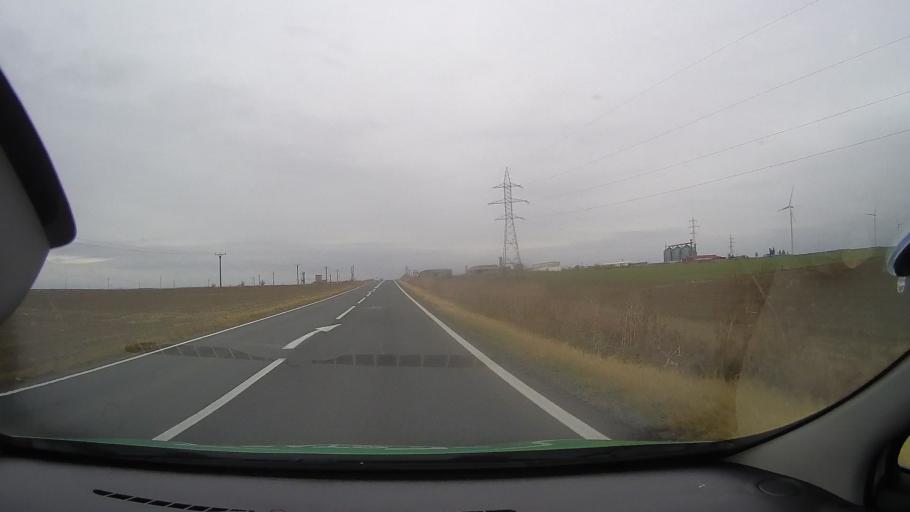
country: RO
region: Constanta
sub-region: Comuna Nicolae Balcescu
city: Dorobantu
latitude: 44.4247
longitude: 28.3095
